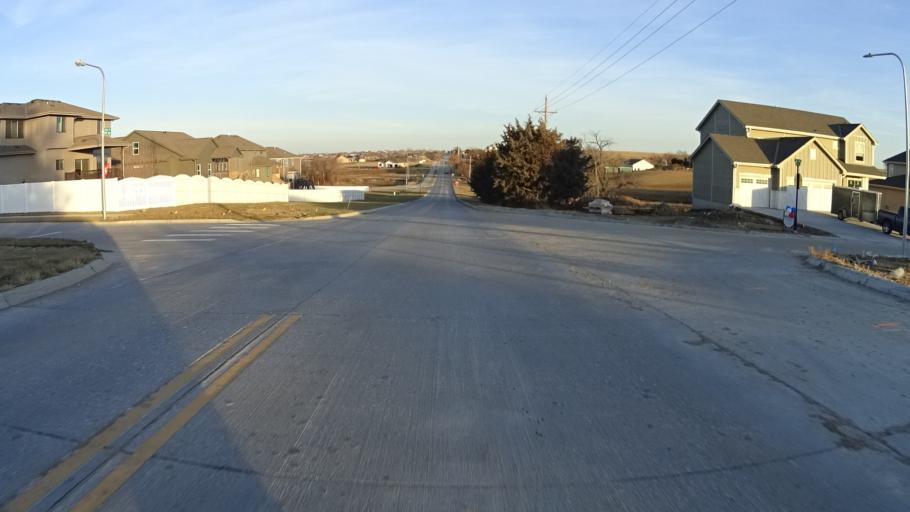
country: US
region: Nebraska
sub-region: Sarpy County
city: Papillion
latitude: 41.1326
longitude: -96.0845
